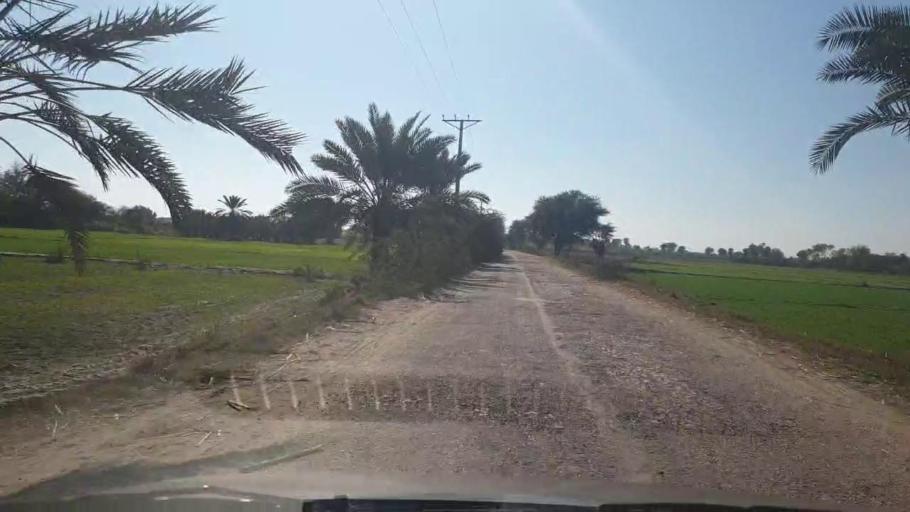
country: PK
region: Sindh
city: Bozdar
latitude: 27.2688
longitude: 68.6517
